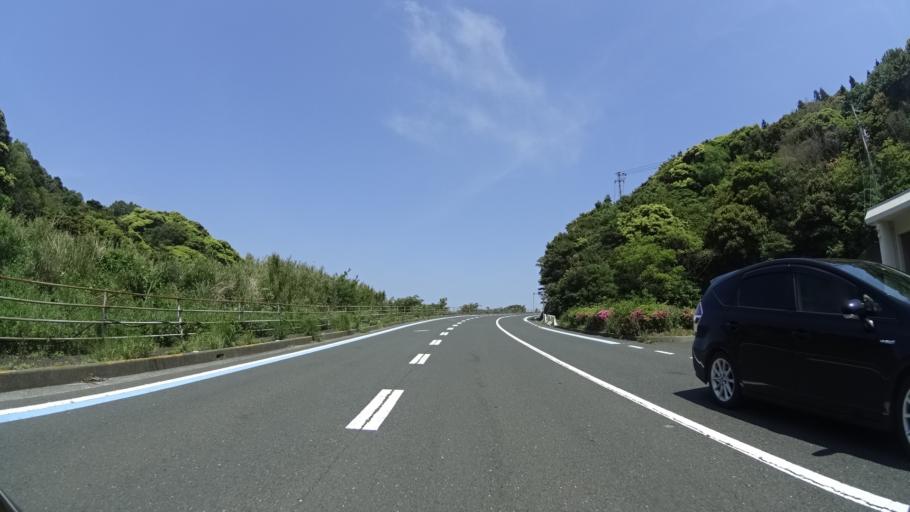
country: JP
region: Ehime
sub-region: Nishiuwa-gun
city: Ikata-cho
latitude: 33.4106
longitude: 132.1728
